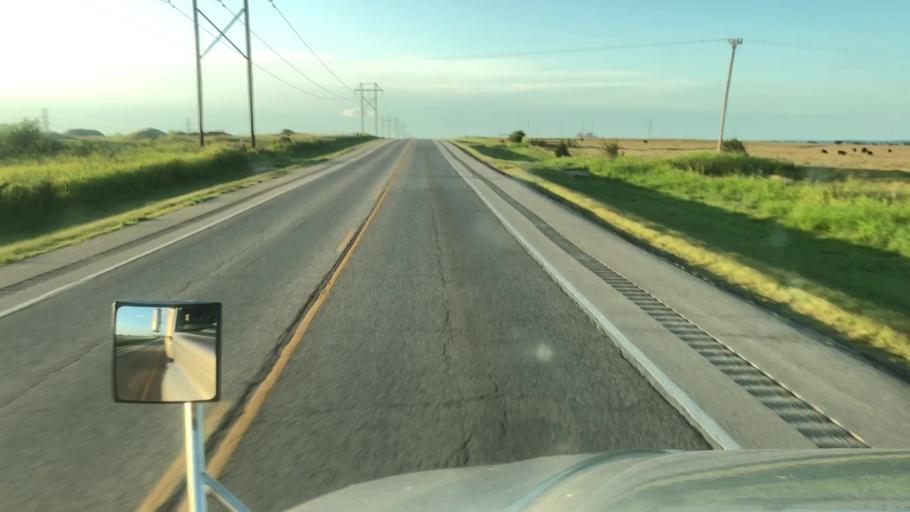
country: US
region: Oklahoma
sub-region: Noble County
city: Perry
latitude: 36.3906
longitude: -97.0677
